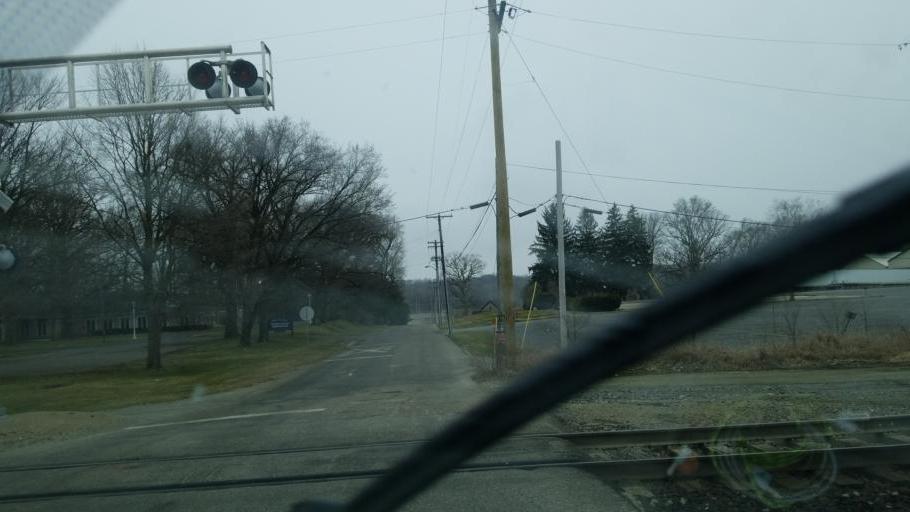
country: US
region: Indiana
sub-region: Wabash County
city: Wabash
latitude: 40.8004
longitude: -85.8424
